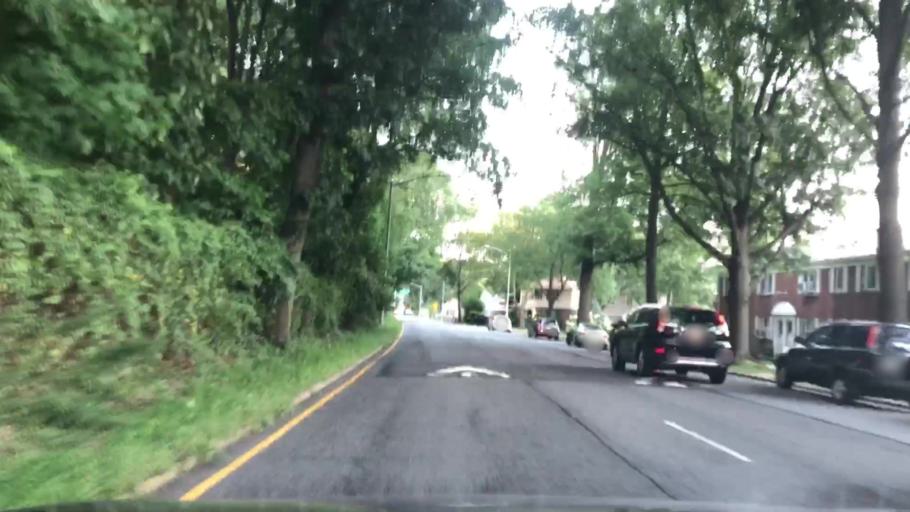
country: US
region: New York
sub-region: Nassau County
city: Bellerose Terrace
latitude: 40.7346
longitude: -73.7426
